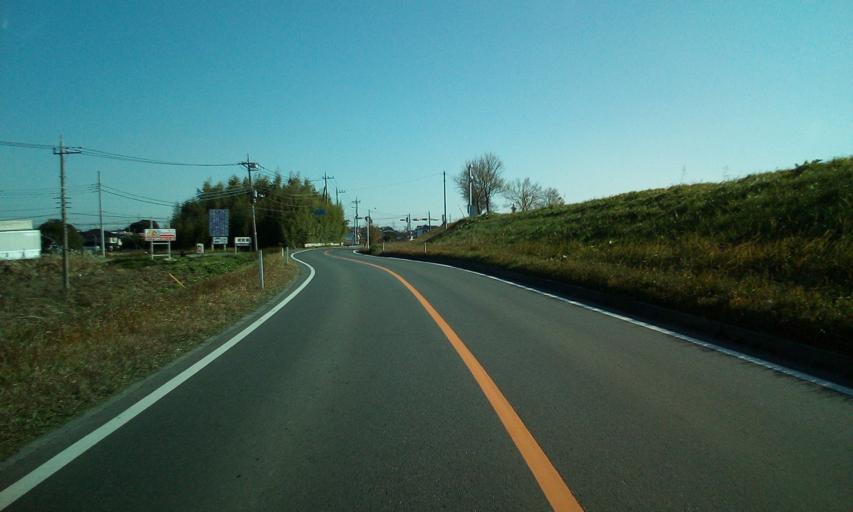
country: JP
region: Ibaraki
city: Sakai
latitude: 36.1084
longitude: 139.7859
